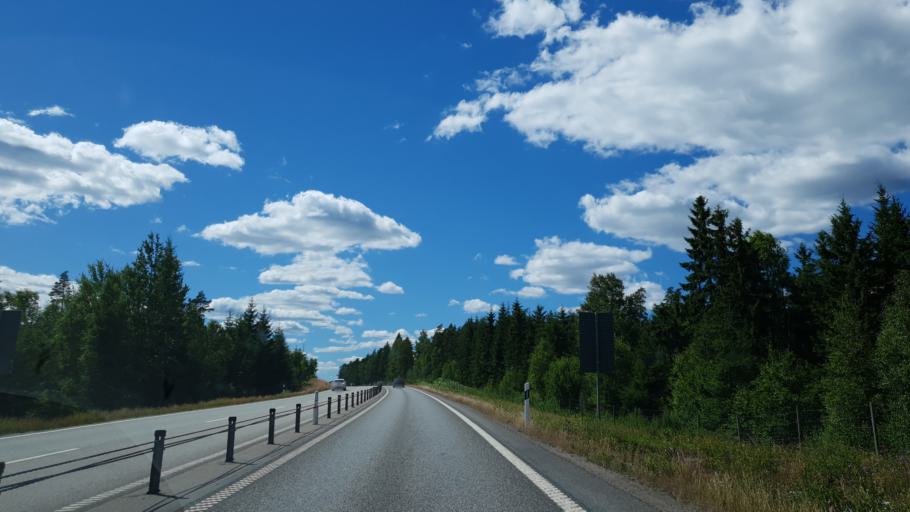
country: SE
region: Kronoberg
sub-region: Vaxjo Kommun
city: Ingelstad
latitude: 56.8702
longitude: 14.9900
